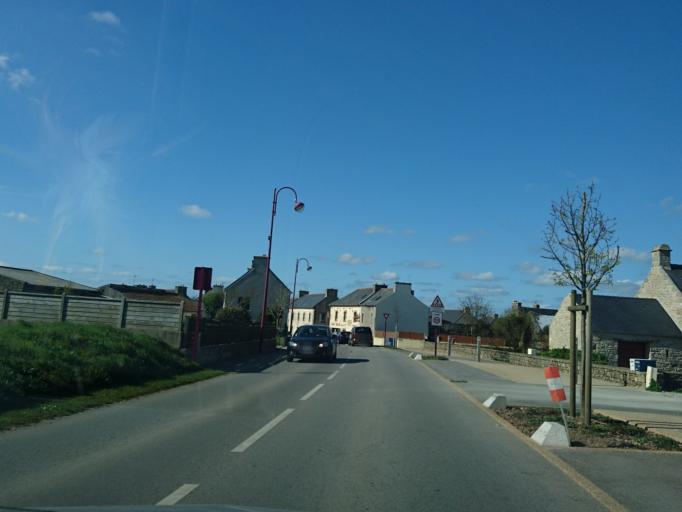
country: FR
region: Brittany
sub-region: Departement du Finistere
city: Lanrivoare
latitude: 48.4727
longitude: -4.6394
